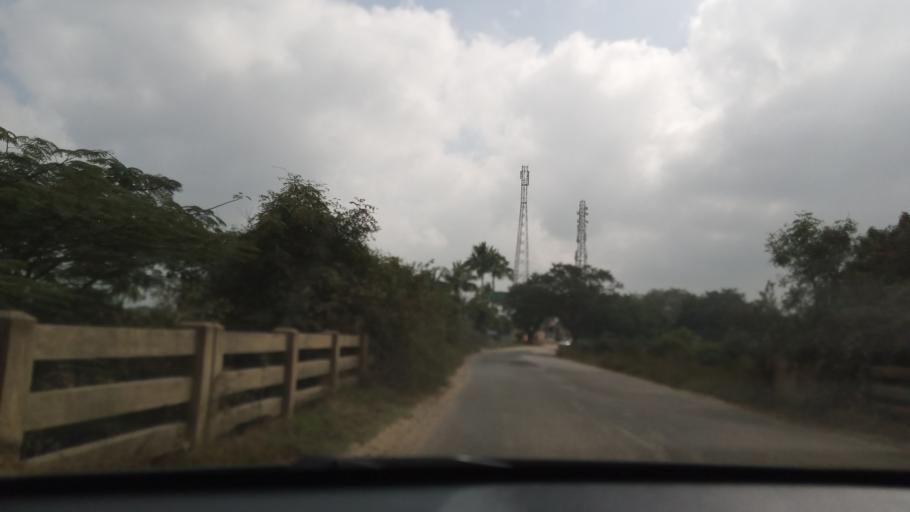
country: IN
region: Karnataka
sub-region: Kolar
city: Srinivaspur
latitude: 13.4394
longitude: 78.2227
